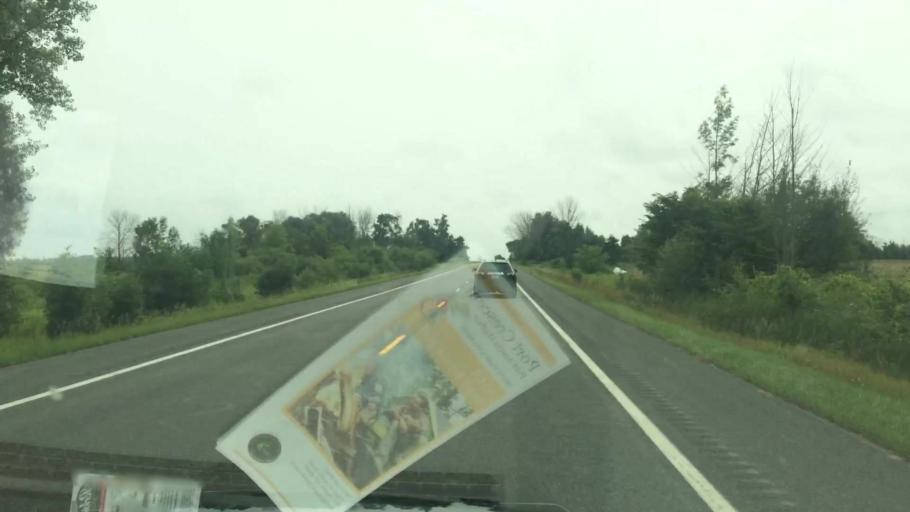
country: US
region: Michigan
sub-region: Huron County
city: Harbor Beach
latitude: 44.0128
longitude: -82.7957
